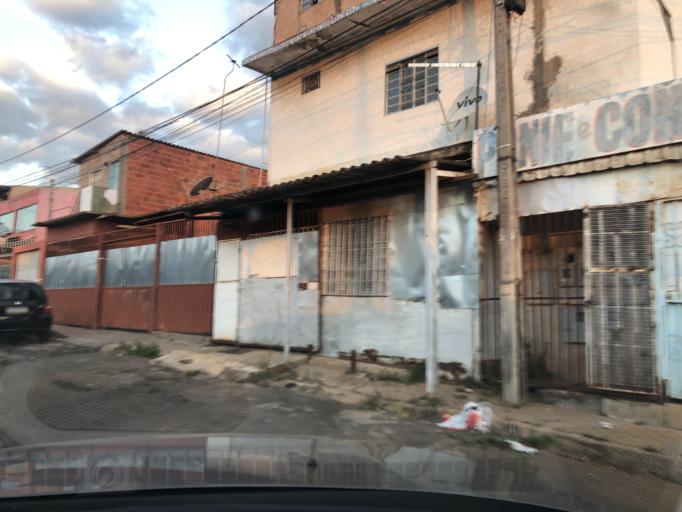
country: BR
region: Federal District
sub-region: Brasilia
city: Brasilia
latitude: -15.8782
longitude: -48.0987
